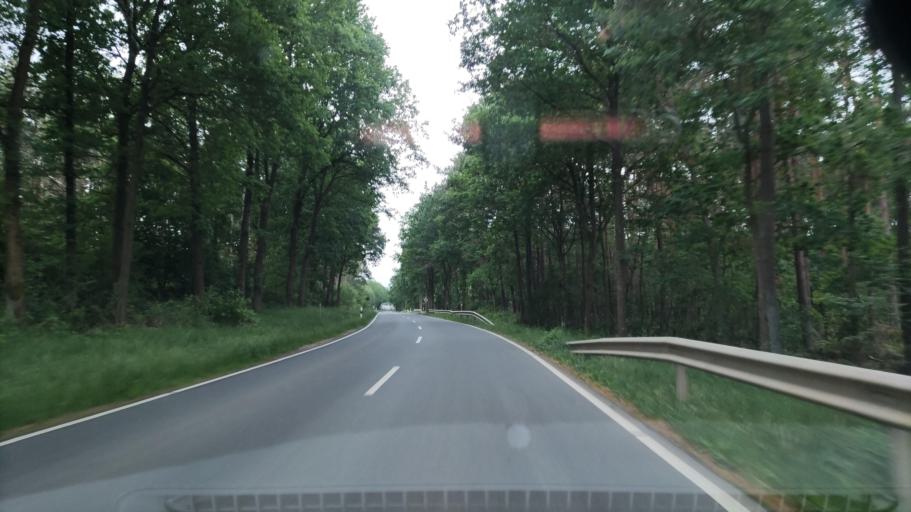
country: DE
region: Lower Saxony
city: Neuenkirchen
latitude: 53.0894
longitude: 9.6692
